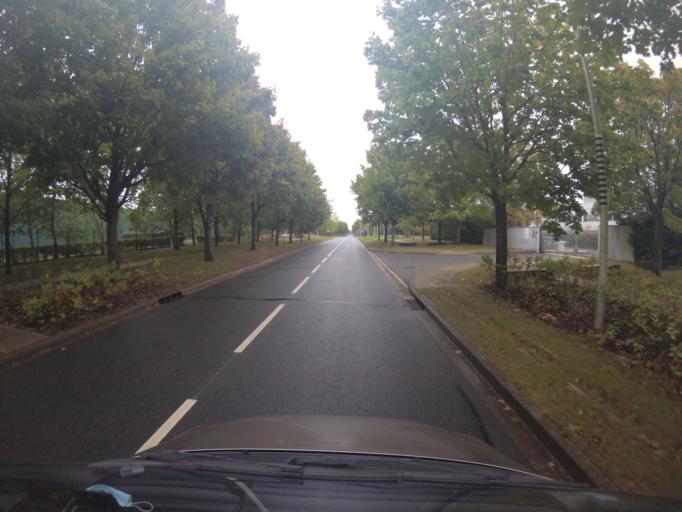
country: FR
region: Ile-de-France
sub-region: Departement de Seine-et-Marne
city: Ferrieres-en-Brie
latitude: 48.8315
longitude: 2.7299
